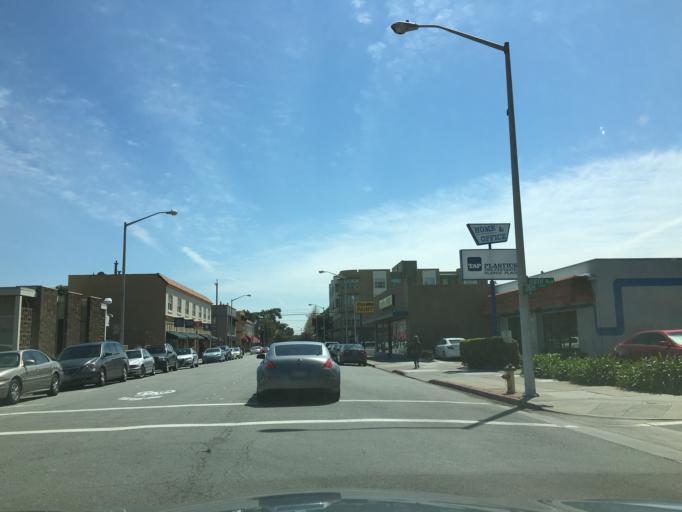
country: US
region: California
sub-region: San Mateo County
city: San Mateo
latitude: 37.5636
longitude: -122.3203
